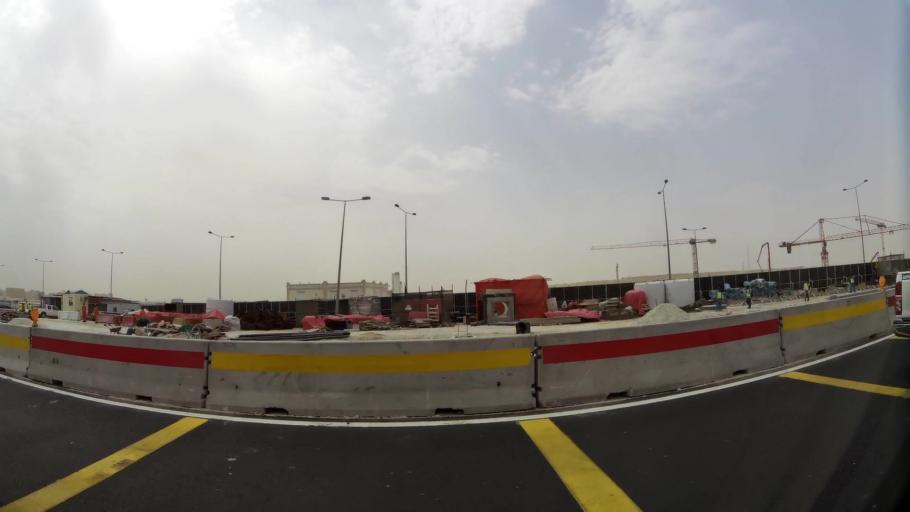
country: QA
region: Baladiyat ad Dawhah
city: Doha
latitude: 25.2938
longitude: 51.4869
